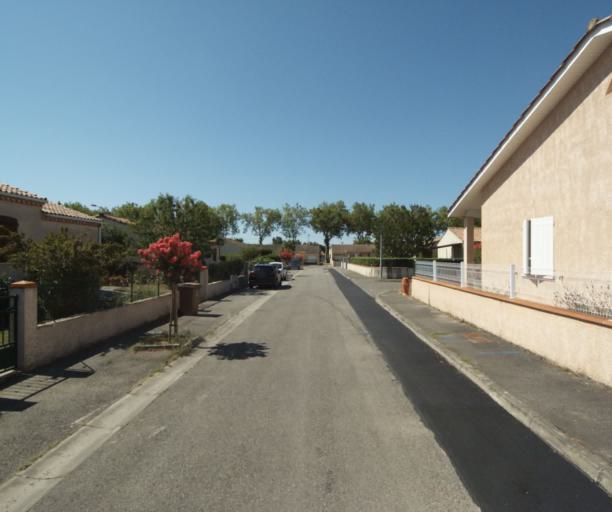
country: FR
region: Midi-Pyrenees
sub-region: Departement de la Haute-Garonne
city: Revel
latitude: 43.4641
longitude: 1.9938
